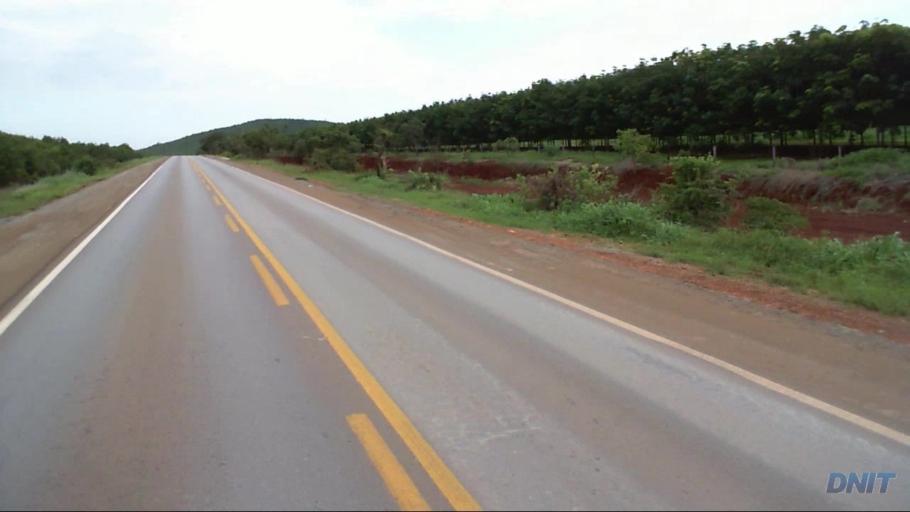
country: BR
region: Goias
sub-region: Barro Alto
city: Barro Alto
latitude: -14.9079
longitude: -48.9593
